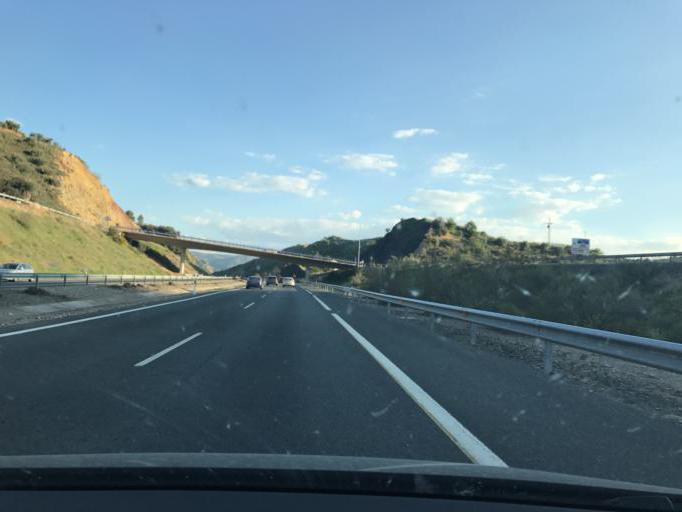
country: ES
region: Andalusia
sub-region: Provincia de Jaen
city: Cambil
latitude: 37.6440
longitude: -3.6072
